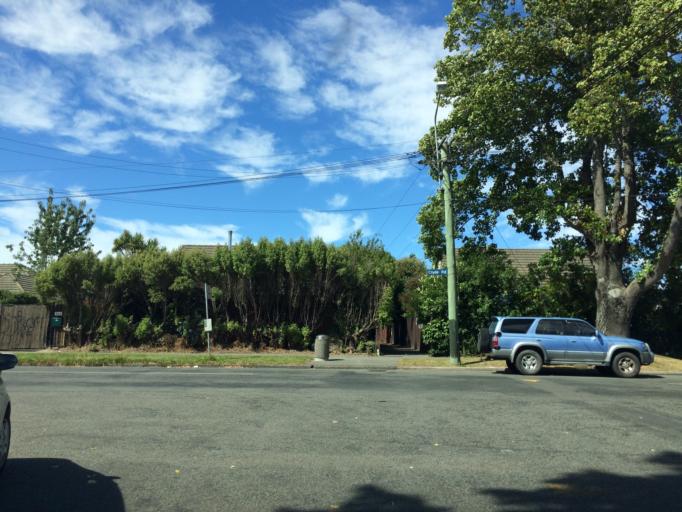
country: NZ
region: Canterbury
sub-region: Christchurch City
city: Christchurch
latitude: -43.5048
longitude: 172.5842
